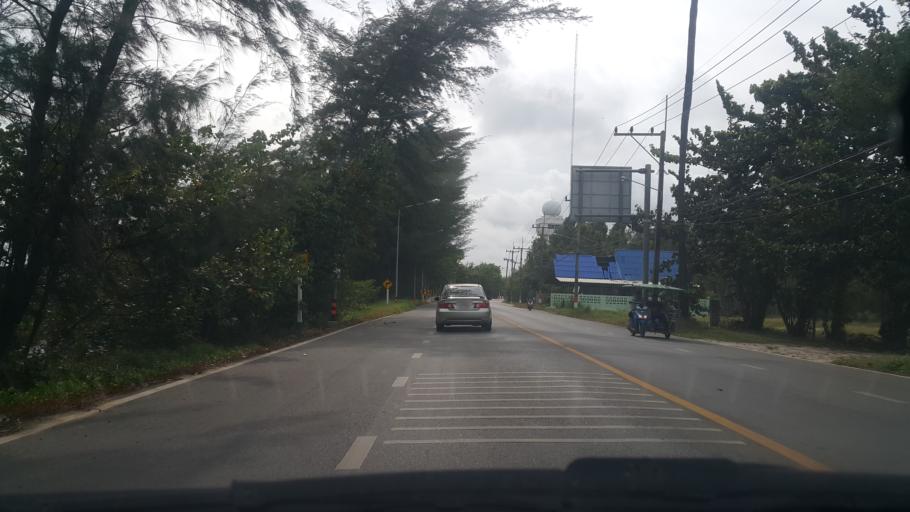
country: TH
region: Rayong
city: Rayong
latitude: 12.6322
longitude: 101.3425
